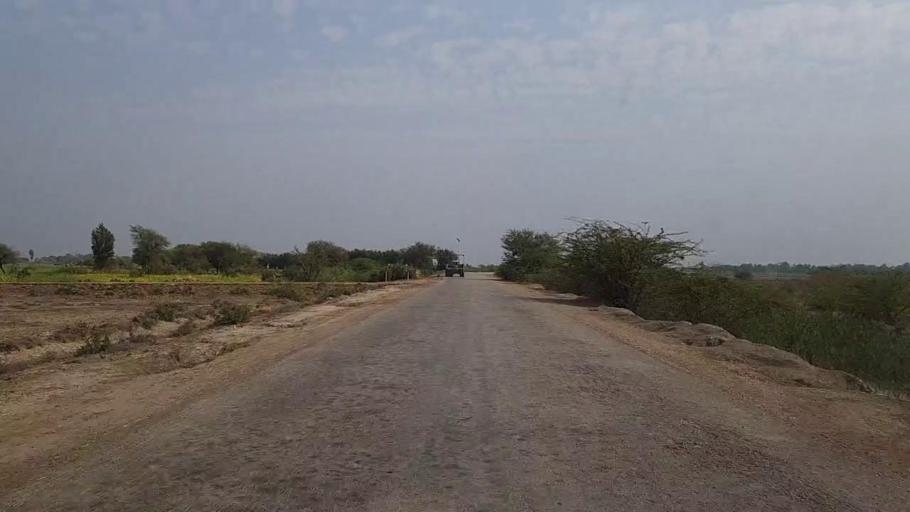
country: PK
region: Sindh
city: Mirwah Gorchani
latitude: 25.4162
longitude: 69.0322
